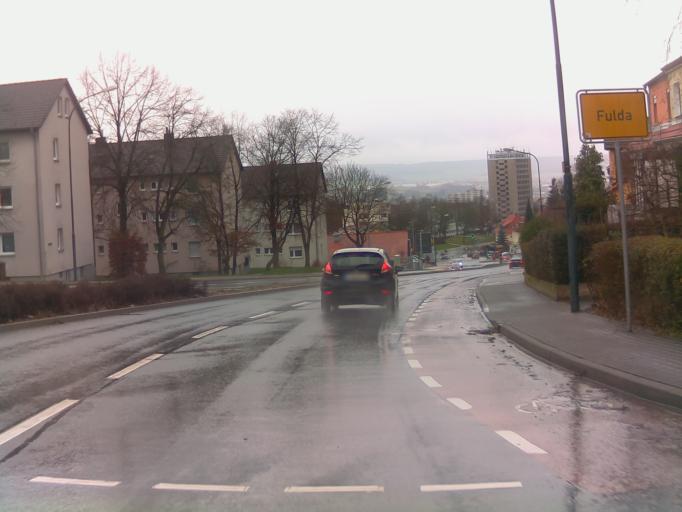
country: DE
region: Hesse
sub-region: Regierungsbezirk Kassel
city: Petersberg
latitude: 50.5532
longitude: 9.7108
